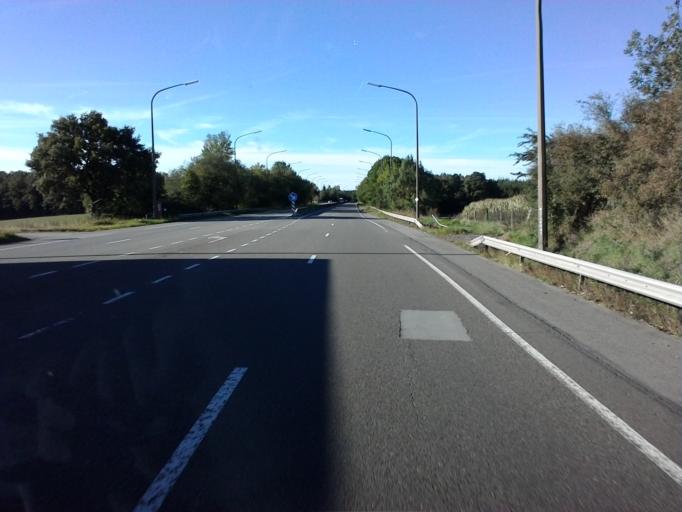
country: BE
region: Wallonia
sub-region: Province du Luxembourg
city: Fauvillers
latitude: 49.8776
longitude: 5.7060
